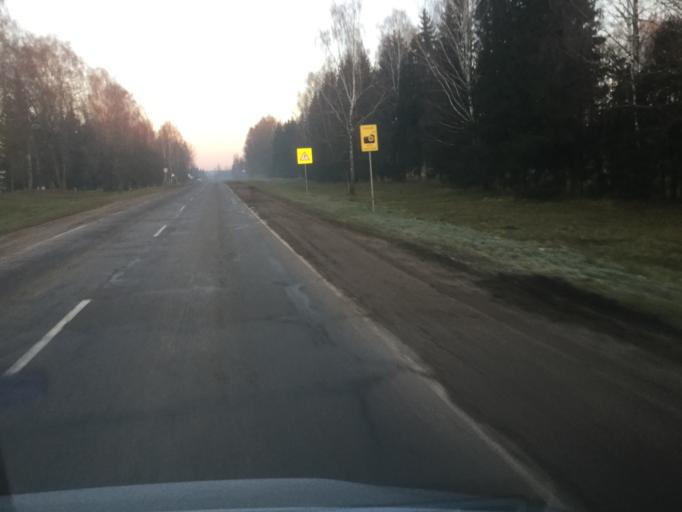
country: BY
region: Vitebsk
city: Vyerkhnyadzvinsk
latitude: 55.7132
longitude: 28.0779
